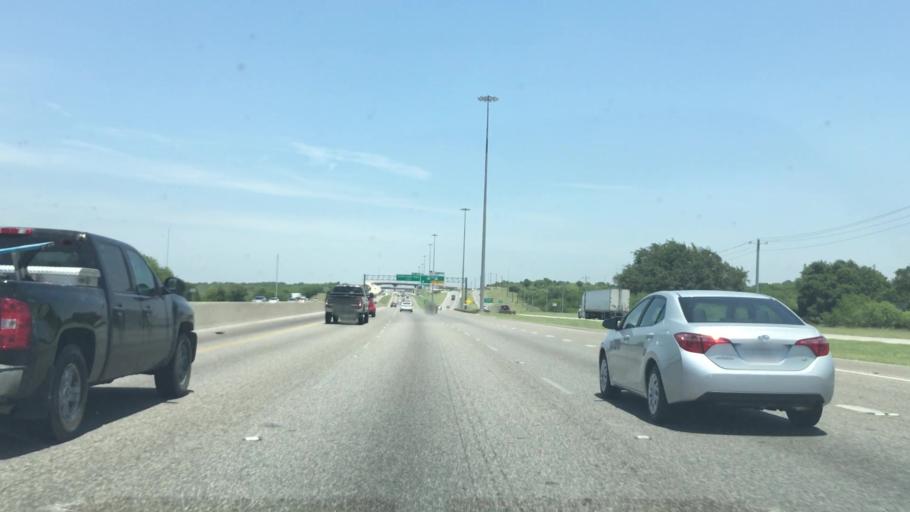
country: US
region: Texas
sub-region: Hays County
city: Buda
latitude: 30.0970
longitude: -97.8141
